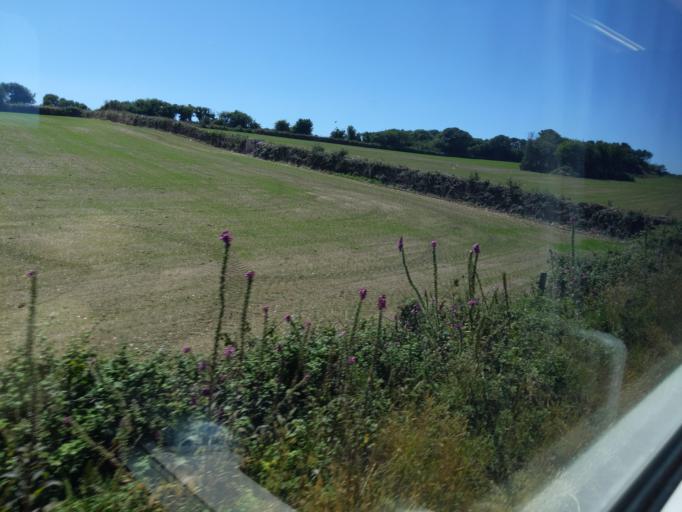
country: GB
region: England
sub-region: Cornwall
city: Chacewater
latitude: 50.2657
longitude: -5.1760
